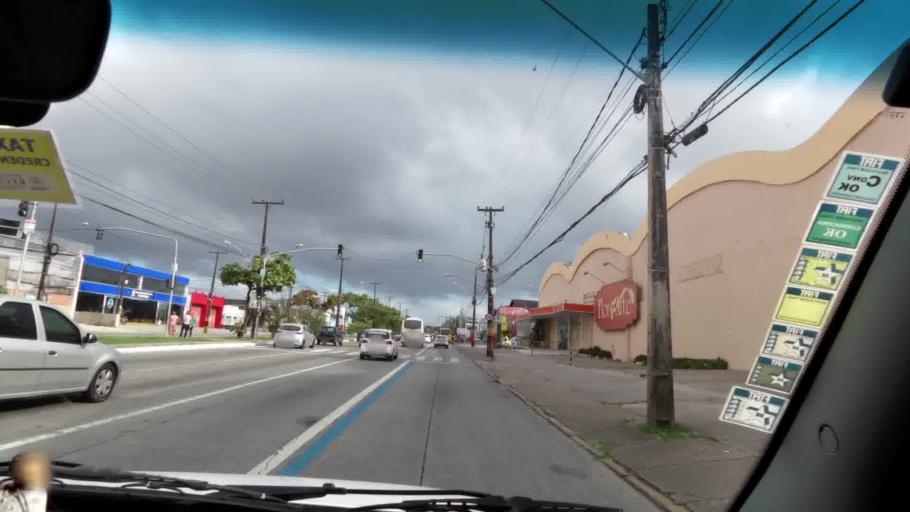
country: BR
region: Pernambuco
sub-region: Recife
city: Recife
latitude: -8.0859
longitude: -34.9068
